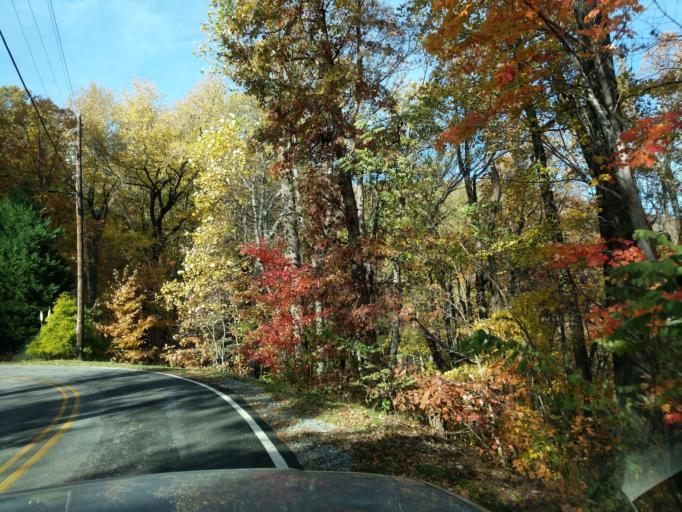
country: US
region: North Carolina
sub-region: Polk County
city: Columbus
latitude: 35.2658
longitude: -82.2086
